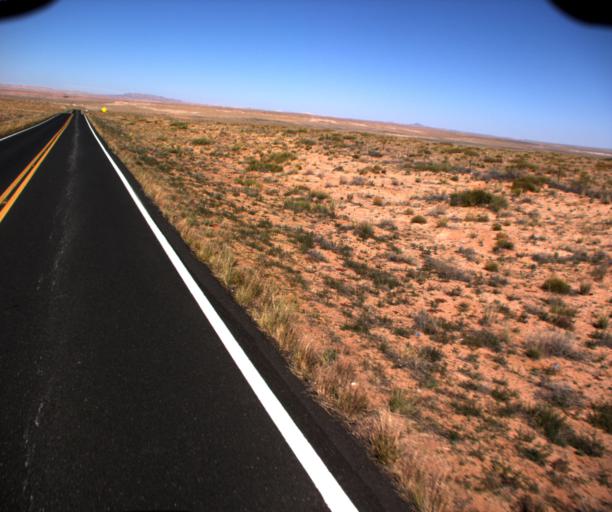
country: US
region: Arizona
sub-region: Coconino County
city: Tuba City
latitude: 36.0769
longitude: -111.1854
